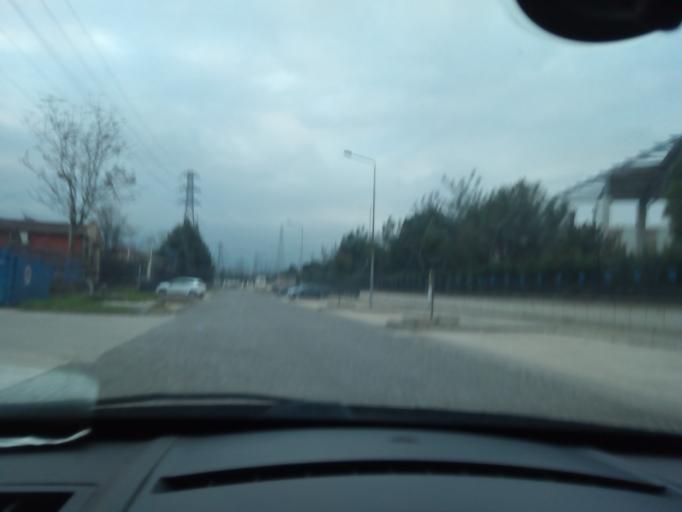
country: TR
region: Bursa
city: Niluefer
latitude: 40.2371
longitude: 28.9683
